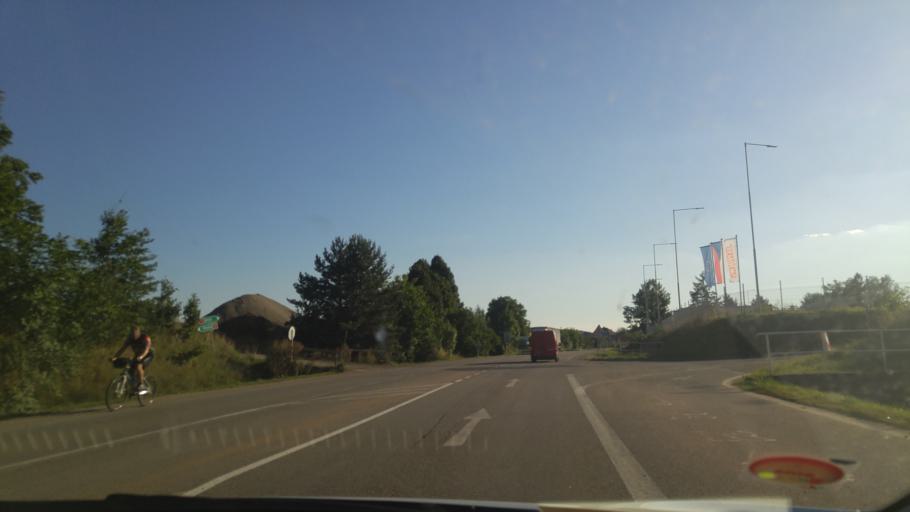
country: CZ
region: South Moravian
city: Ricany
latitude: 49.2154
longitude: 16.4102
